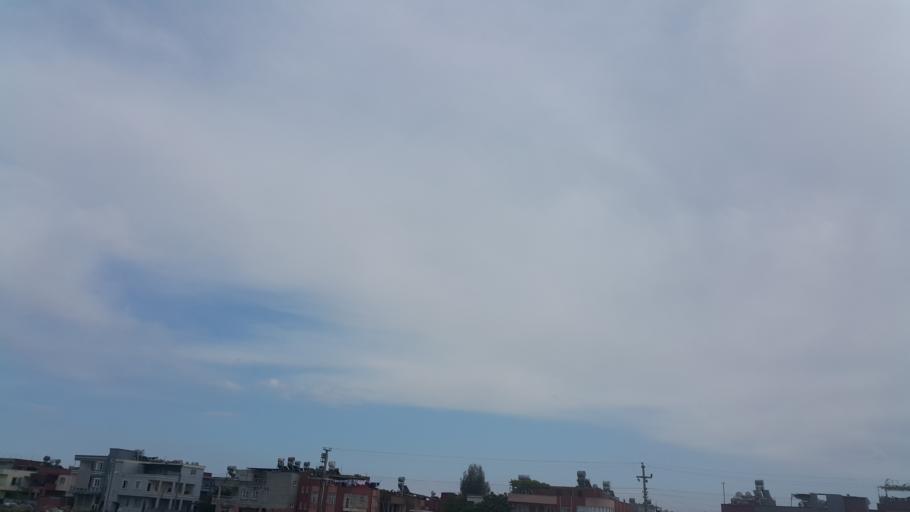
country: TR
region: Mersin
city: Tarsus
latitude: 36.9149
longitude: 34.9179
